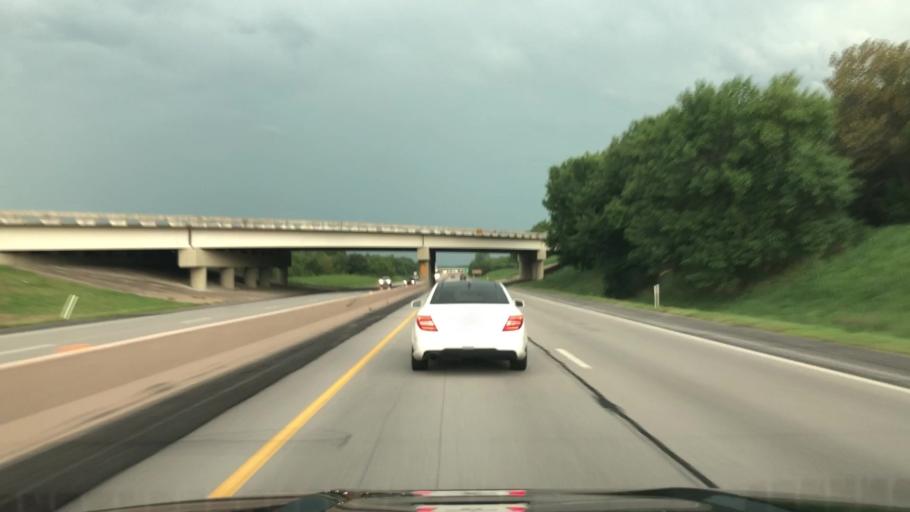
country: US
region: Oklahoma
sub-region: Rogers County
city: Justice
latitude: 36.3078
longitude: -95.5763
